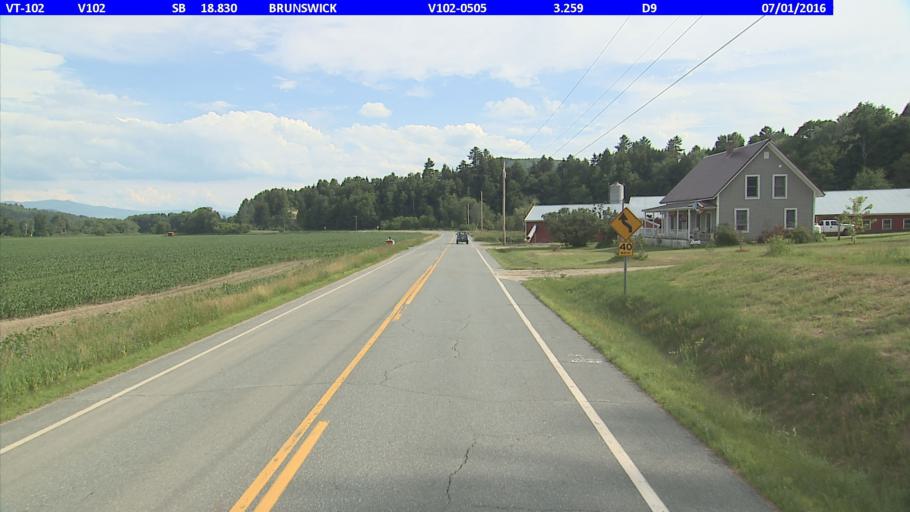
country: US
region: New Hampshire
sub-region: Coos County
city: Stratford
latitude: 44.7055
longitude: -71.6057
